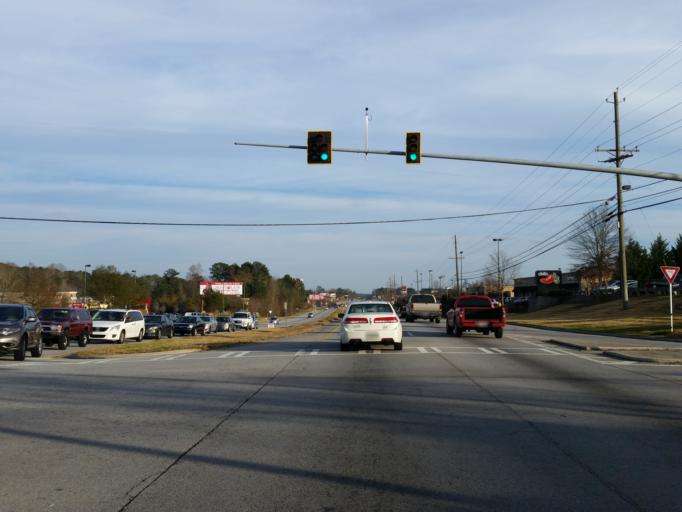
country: US
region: Georgia
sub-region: Paulding County
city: Hiram
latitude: 33.8883
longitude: -84.7453
